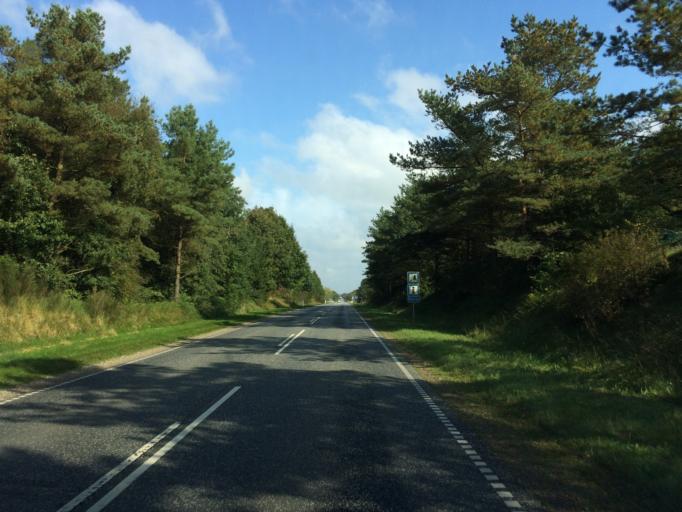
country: DK
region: Central Jutland
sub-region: Skive Kommune
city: Skive
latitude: 56.5235
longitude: 8.9651
